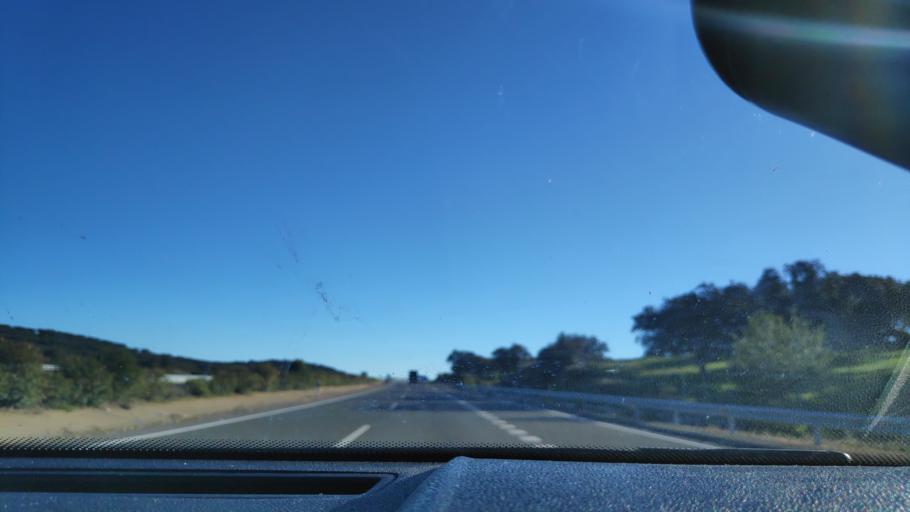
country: ES
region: Extremadura
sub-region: Provincia de Badajoz
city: Monesterio
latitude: 38.1295
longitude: -6.2732
